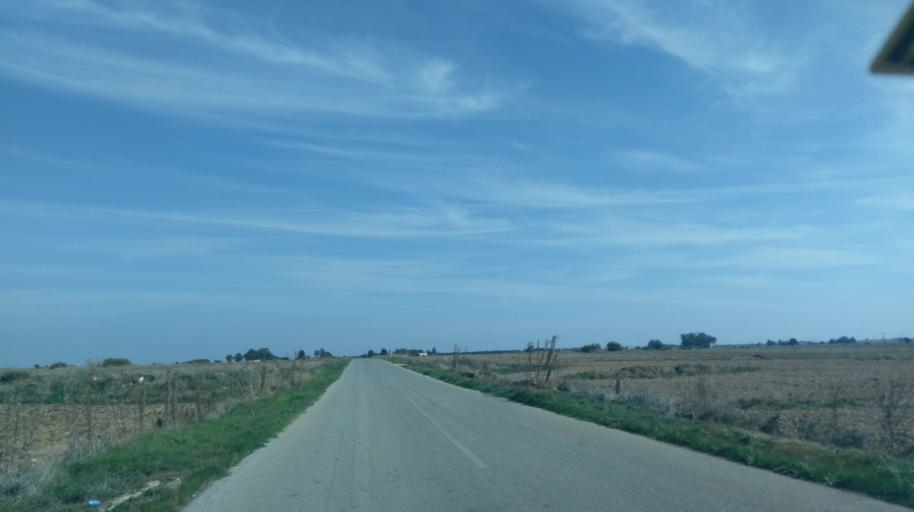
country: CY
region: Ammochostos
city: Lefkonoiko
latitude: 35.2118
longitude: 33.8080
